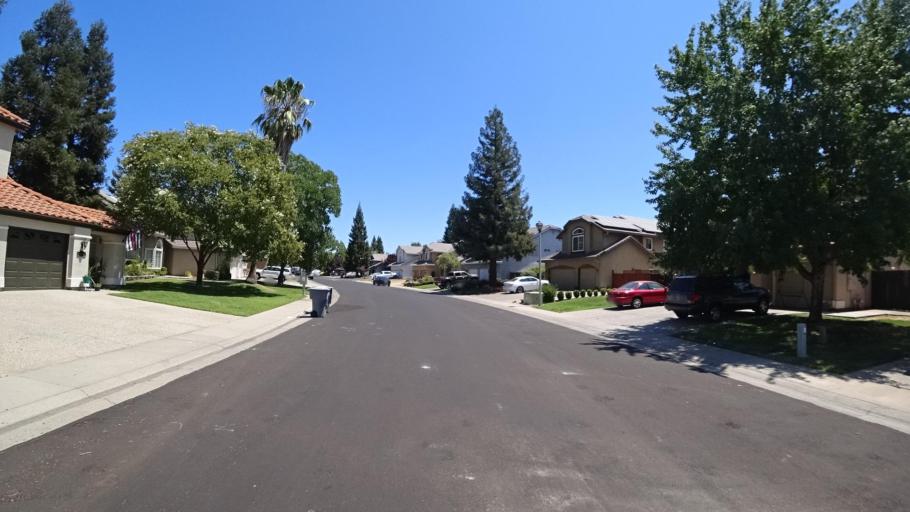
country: US
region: California
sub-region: Placer County
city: Rocklin
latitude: 38.8195
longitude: -121.2623
